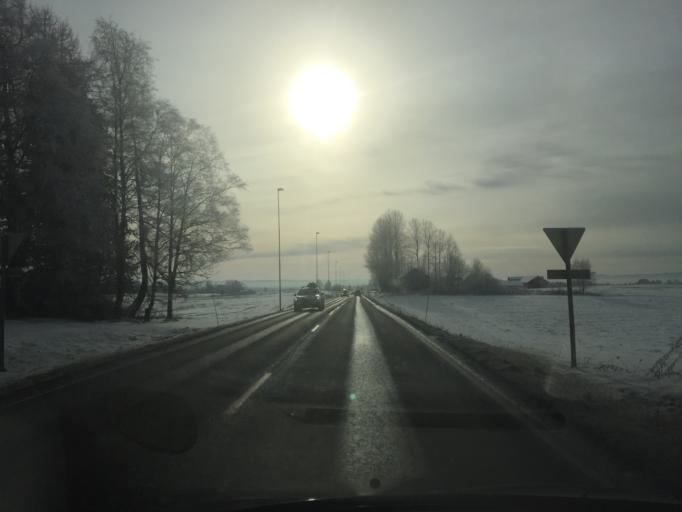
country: NO
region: Hedmark
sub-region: Loten
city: Loten
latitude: 60.8456
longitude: 11.3648
